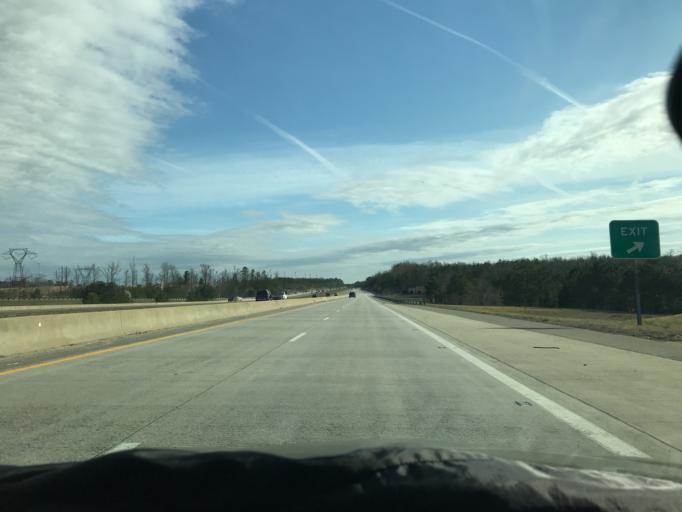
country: US
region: Virginia
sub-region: Chesterfield County
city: Brandermill
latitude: 37.4605
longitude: -77.6385
